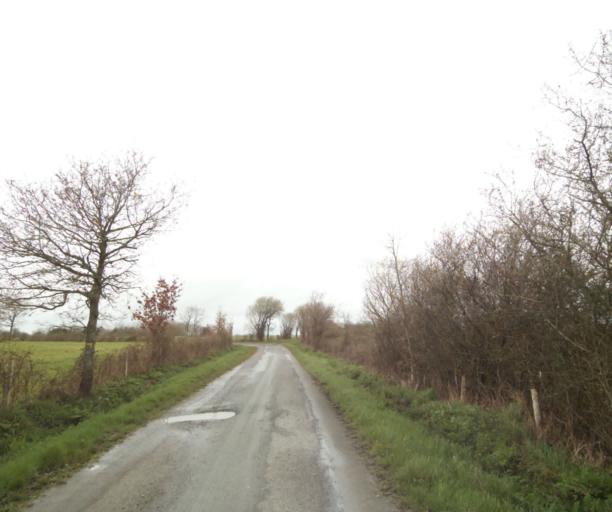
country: FR
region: Pays de la Loire
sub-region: Departement de la Loire-Atlantique
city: Bouvron
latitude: 47.4381
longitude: -1.8769
